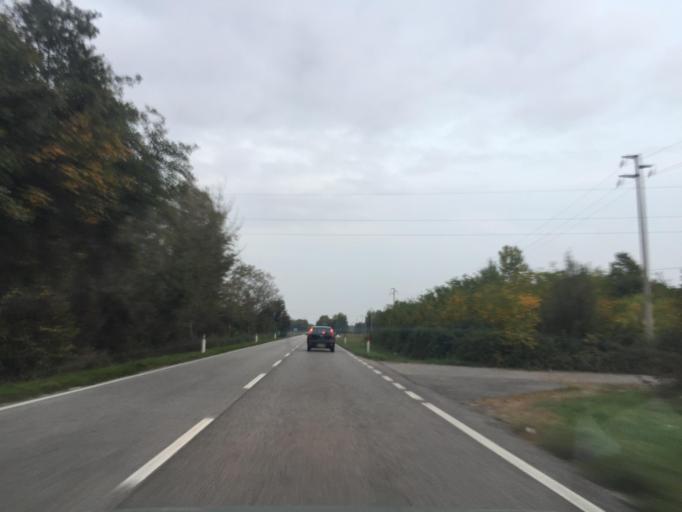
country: IT
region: Friuli Venezia Giulia
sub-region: Provincia di Pordenone
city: Fanna
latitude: 46.1728
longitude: 12.7367
